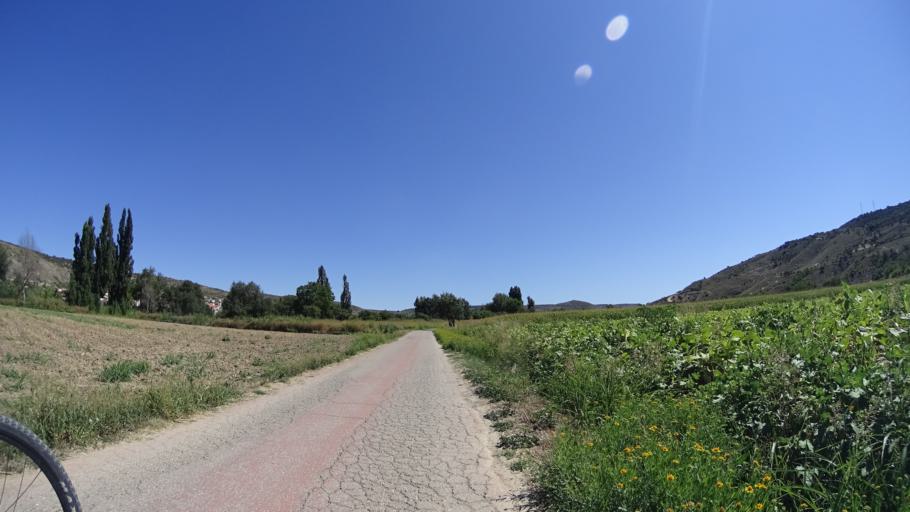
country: ES
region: Madrid
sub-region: Provincia de Madrid
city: Tielmes
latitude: 40.2376
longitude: -3.3181
